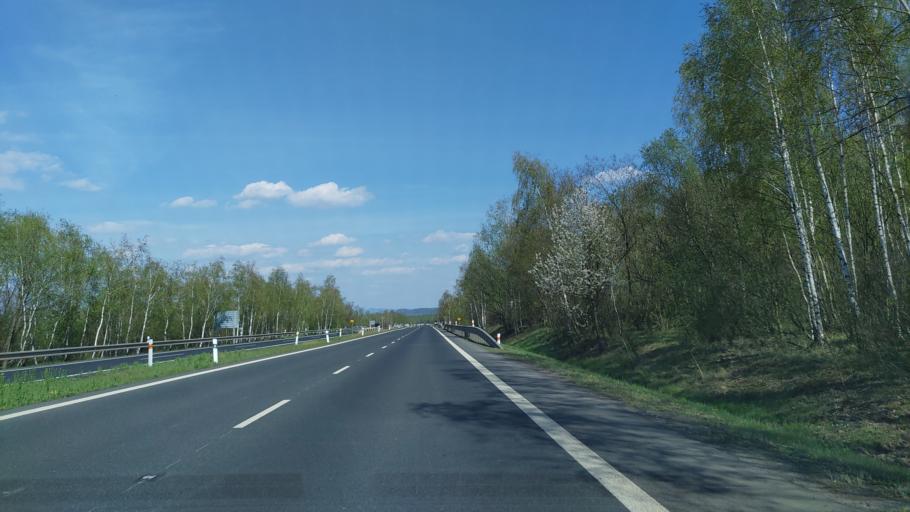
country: CZ
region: Ustecky
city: Jirkov
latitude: 50.5114
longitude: 13.4874
